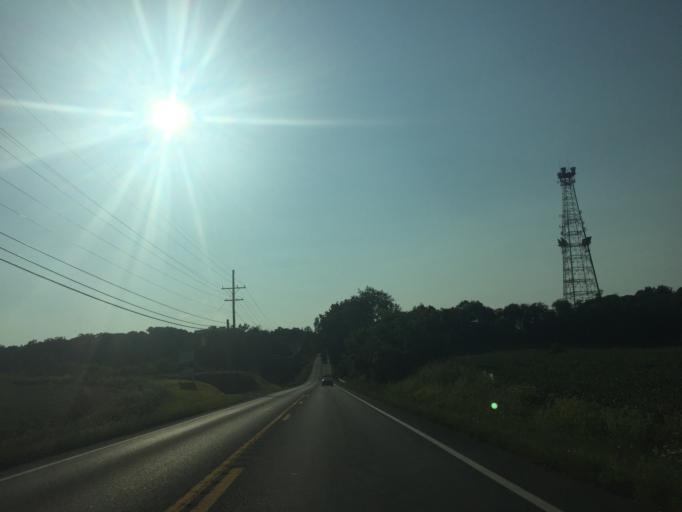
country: US
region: Maryland
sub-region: Frederick County
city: Green Valley
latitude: 39.3473
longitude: -77.2764
